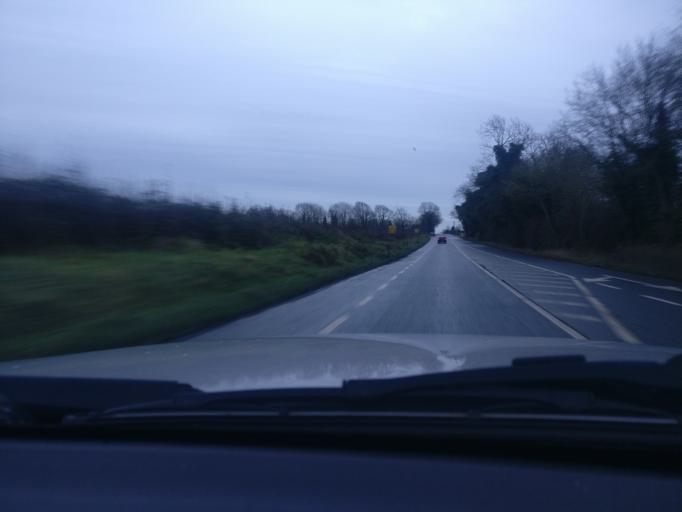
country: IE
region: Leinster
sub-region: An Mhi
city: Navan
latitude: 53.6857
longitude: -6.7669
